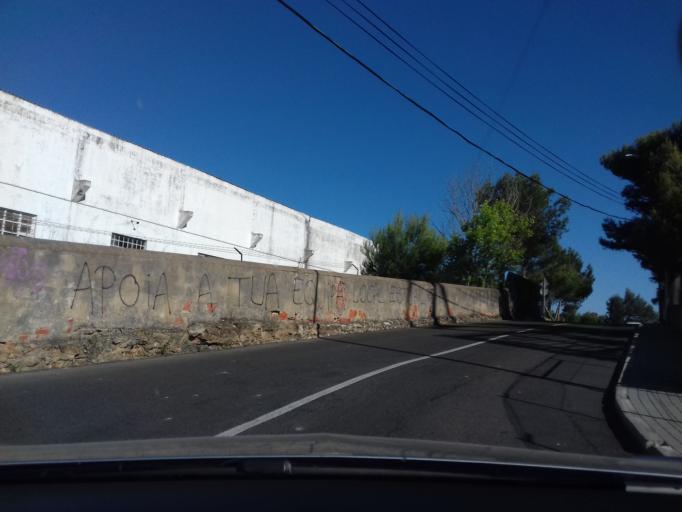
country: PT
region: Lisbon
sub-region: Cascais
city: Alcabideche
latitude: 38.7250
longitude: -9.4140
